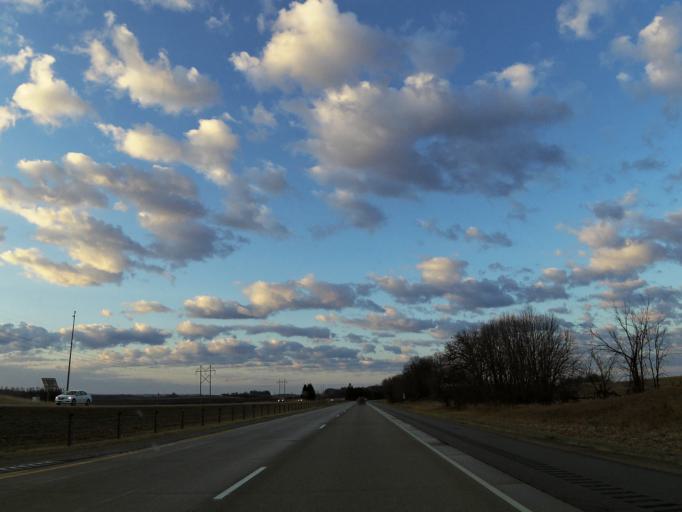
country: US
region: Minnesota
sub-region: Rice County
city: Dundas
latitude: 44.3913
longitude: -93.2927
